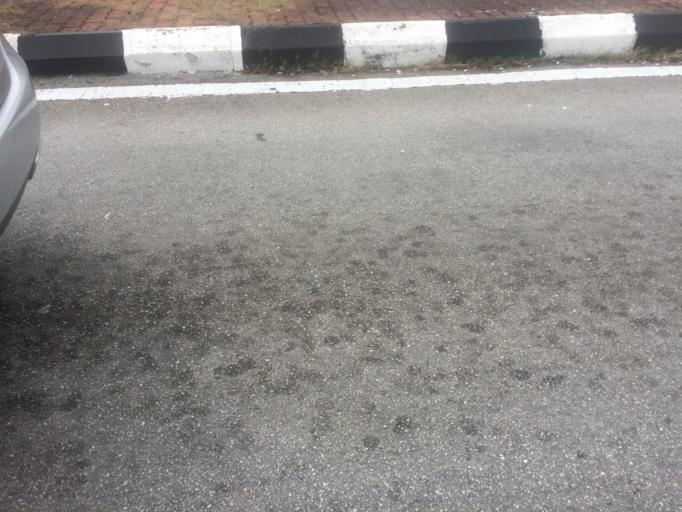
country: MY
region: Perak
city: Ipoh
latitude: 4.6001
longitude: 101.0866
